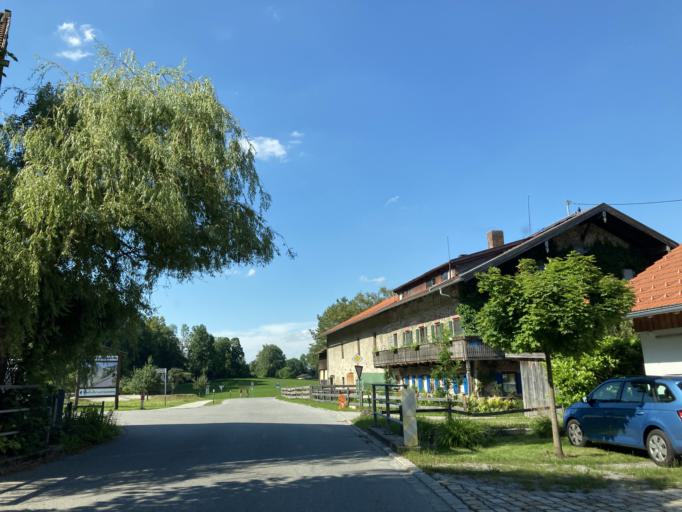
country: DE
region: Bavaria
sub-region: Upper Bavaria
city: Brannenburg
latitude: 47.7252
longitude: 12.0942
